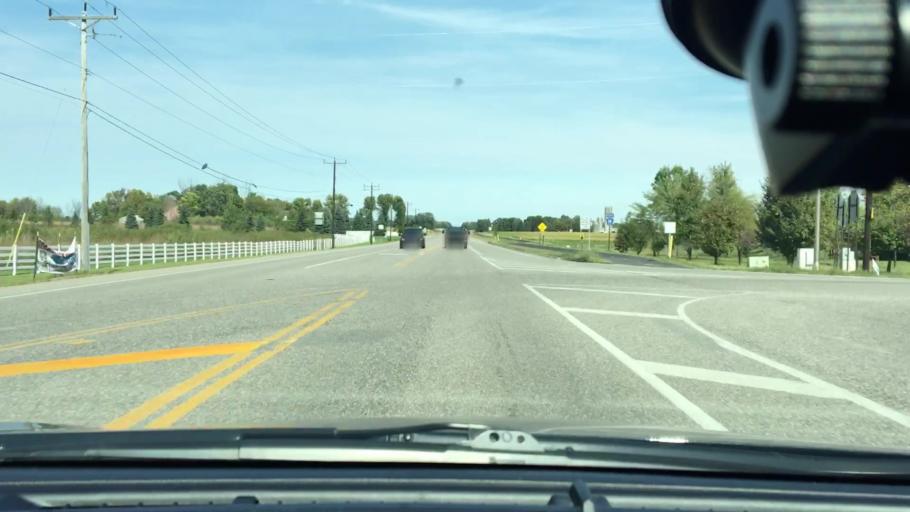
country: US
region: Minnesota
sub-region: Wright County
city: Hanover
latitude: 45.1307
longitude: -93.6357
